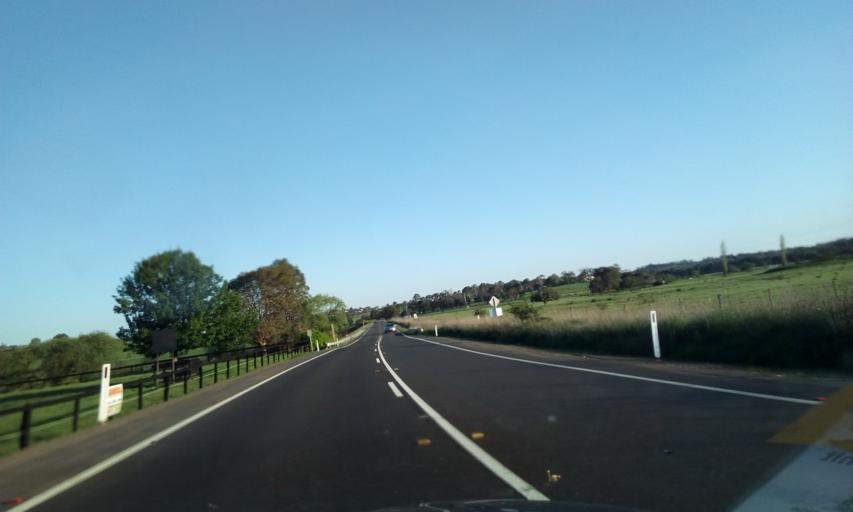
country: AU
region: New South Wales
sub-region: Wollondilly
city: Douglas Park
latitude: -34.1334
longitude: 150.7105
